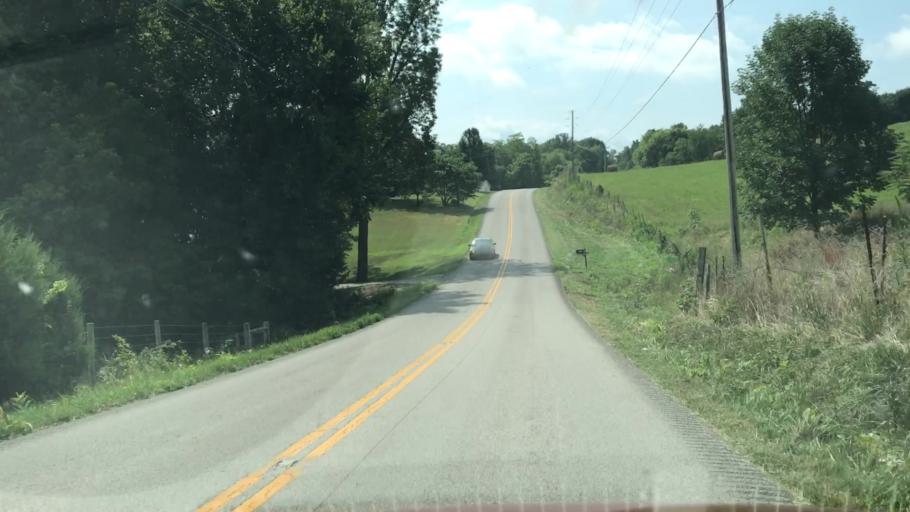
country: US
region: Kentucky
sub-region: Barren County
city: Glasgow
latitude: 36.9036
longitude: -85.8659
